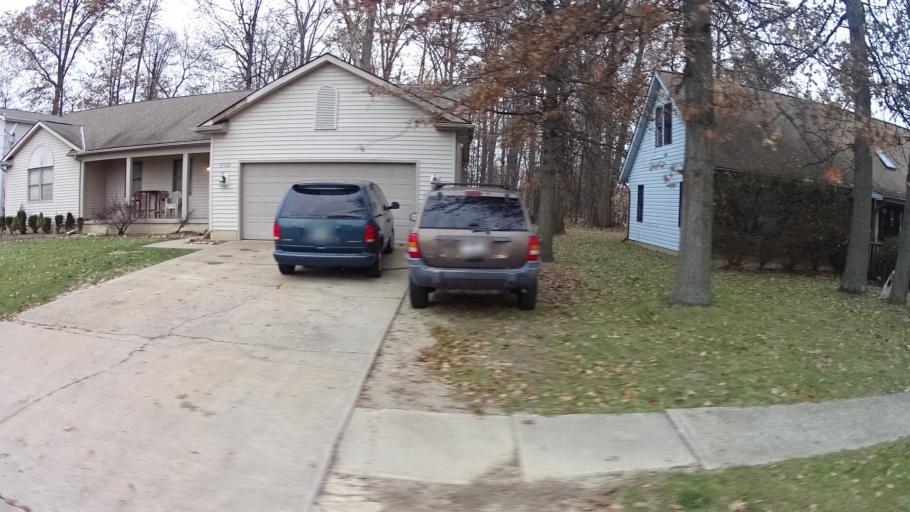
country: US
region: Ohio
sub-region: Lorain County
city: North Ridgeville
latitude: 41.4052
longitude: -82.0116
